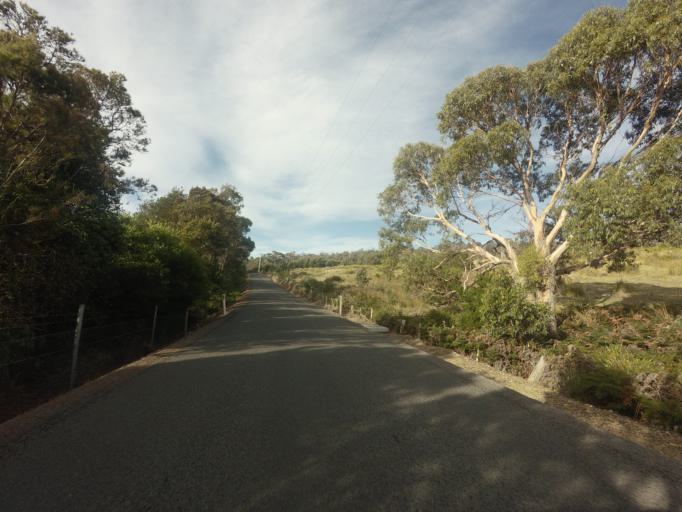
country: AU
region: Tasmania
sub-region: Sorell
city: Sorell
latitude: -42.9637
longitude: 147.8339
